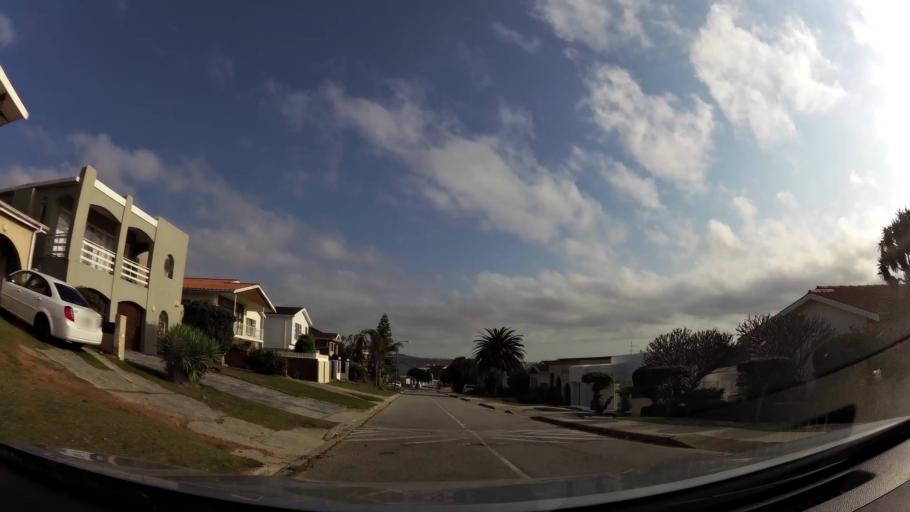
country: ZA
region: Eastern Cape
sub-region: Nelson Mandela Bay Metropolitan Municipality
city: Port Elizabeth
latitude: -33.9273
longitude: 25.5559
